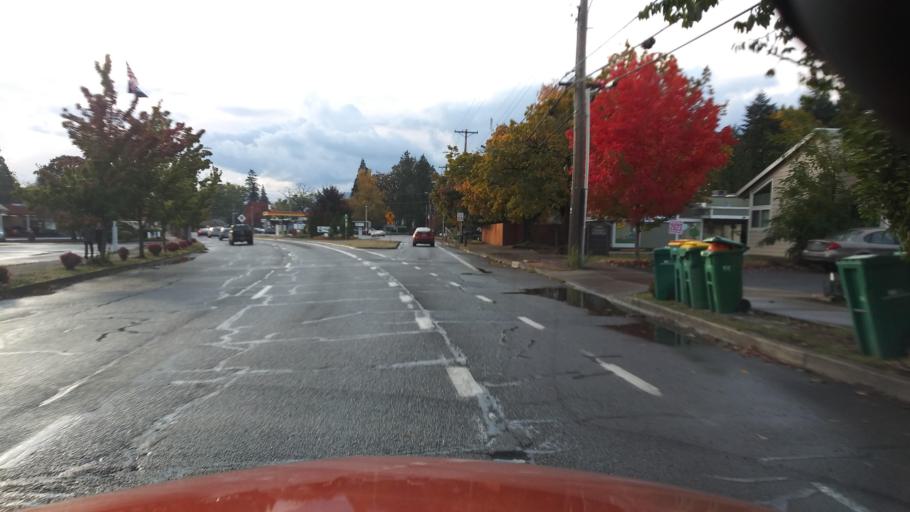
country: US
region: Oregon
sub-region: Washington County
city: Forest Grove
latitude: 45.5202
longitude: -123.0964
